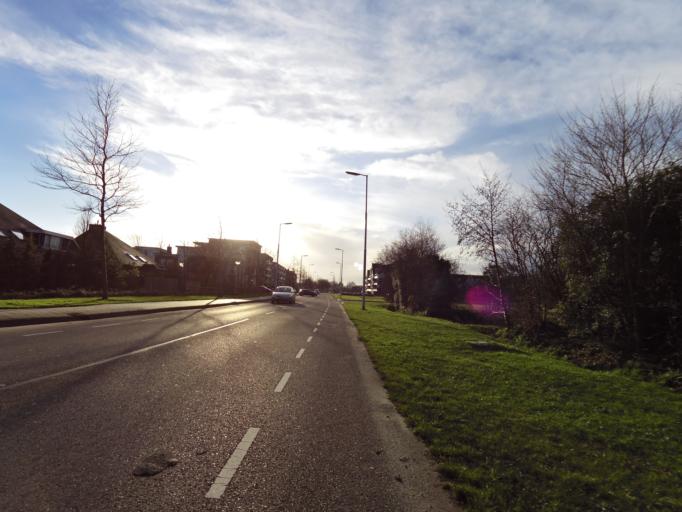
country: NL
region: South Holland
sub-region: Gemeente Brielle
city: Brielle
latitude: 51.9155
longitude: 4.1066
